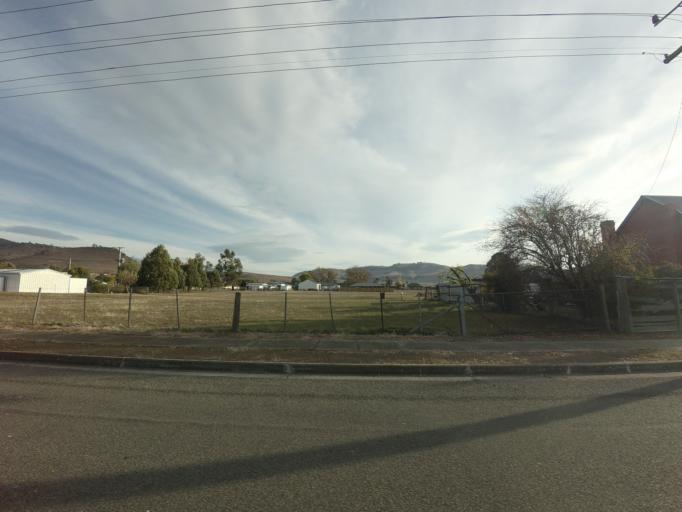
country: AU
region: Tasmania
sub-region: Brighton
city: Bridgewater
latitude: -42.5261
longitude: 147.1969
